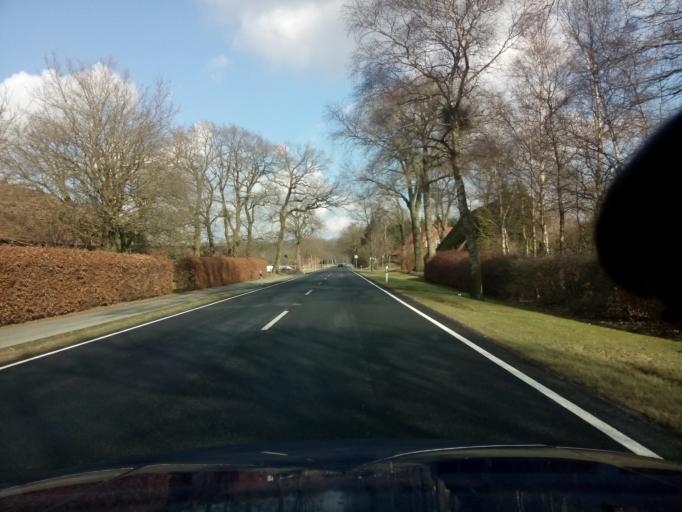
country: DE
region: Lower Saxony
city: Vollersode
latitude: 53.3697
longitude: 8.9441
